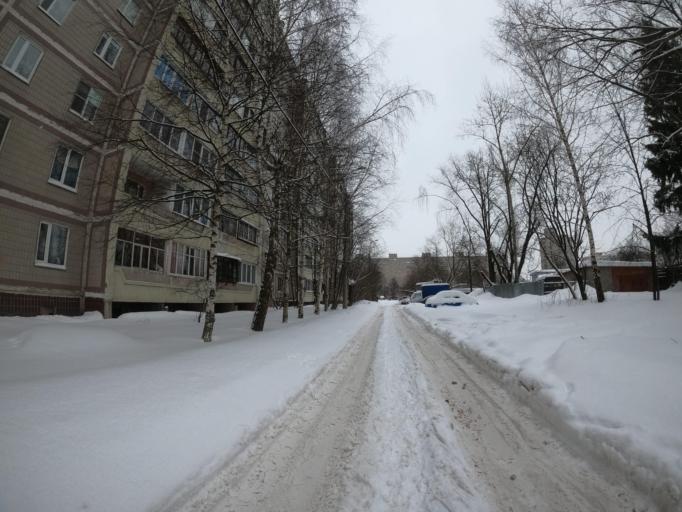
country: RU
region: Moskovskaya
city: Vostryakovo
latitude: 55.4153
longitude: 37.8298
